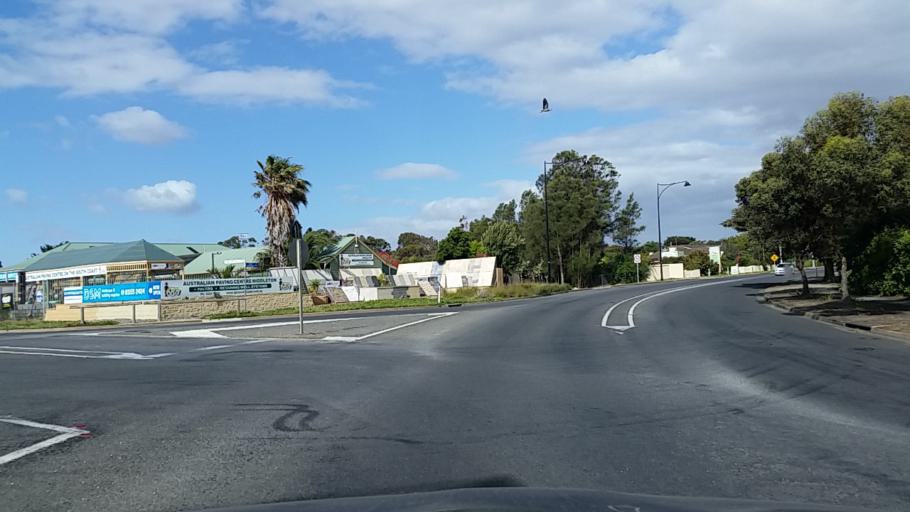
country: AU
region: South Australia
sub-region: Alexandrina
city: Port Elliot
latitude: -35.5076
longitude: 138.7092
